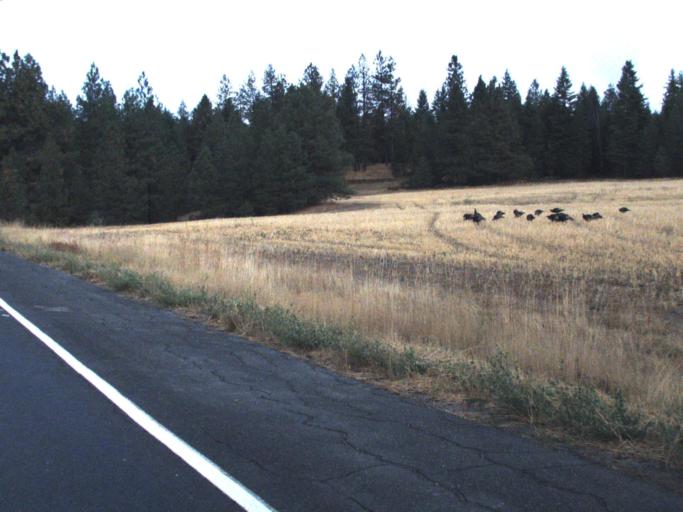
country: US
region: Washington
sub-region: Stevens County
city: Chewelah
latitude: 48.0645
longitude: -117.6845
